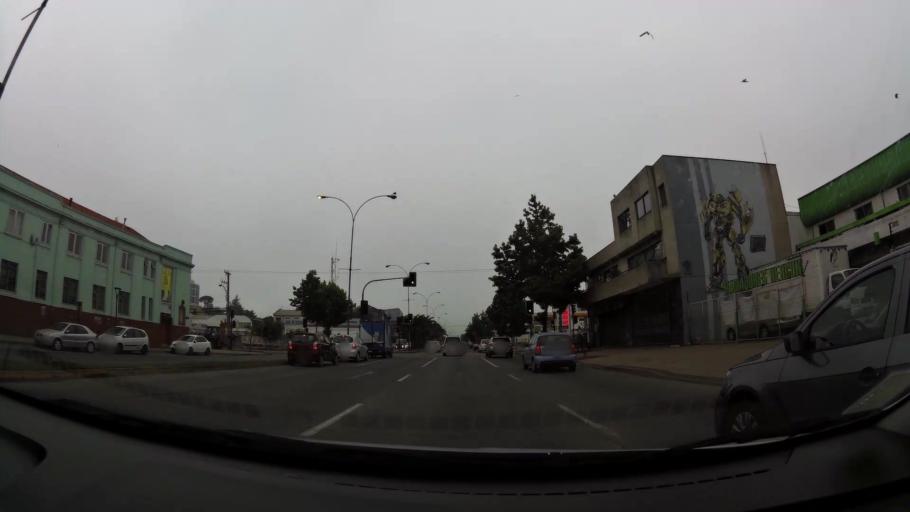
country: CL
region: Biobio
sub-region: Provincia de Concepcion
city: Concepcion
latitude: -36.8261
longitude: -73.0585
